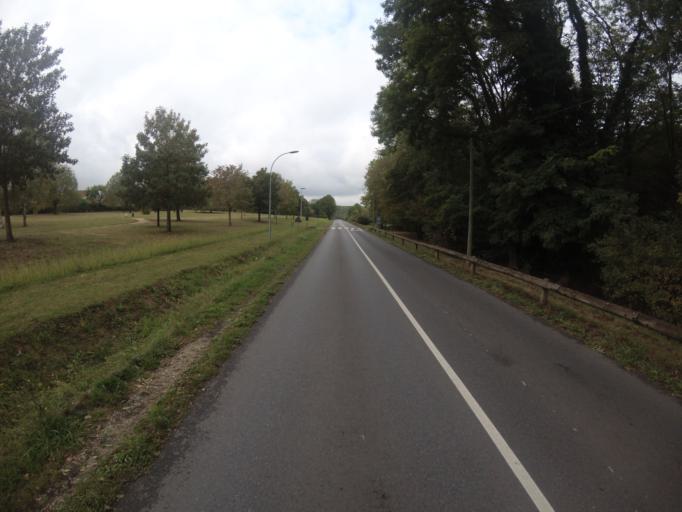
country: FR
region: Ile-de-France
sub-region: Departement de Seine-et-Marne
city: Montevrain
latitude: 48.8704
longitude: 2.7480
